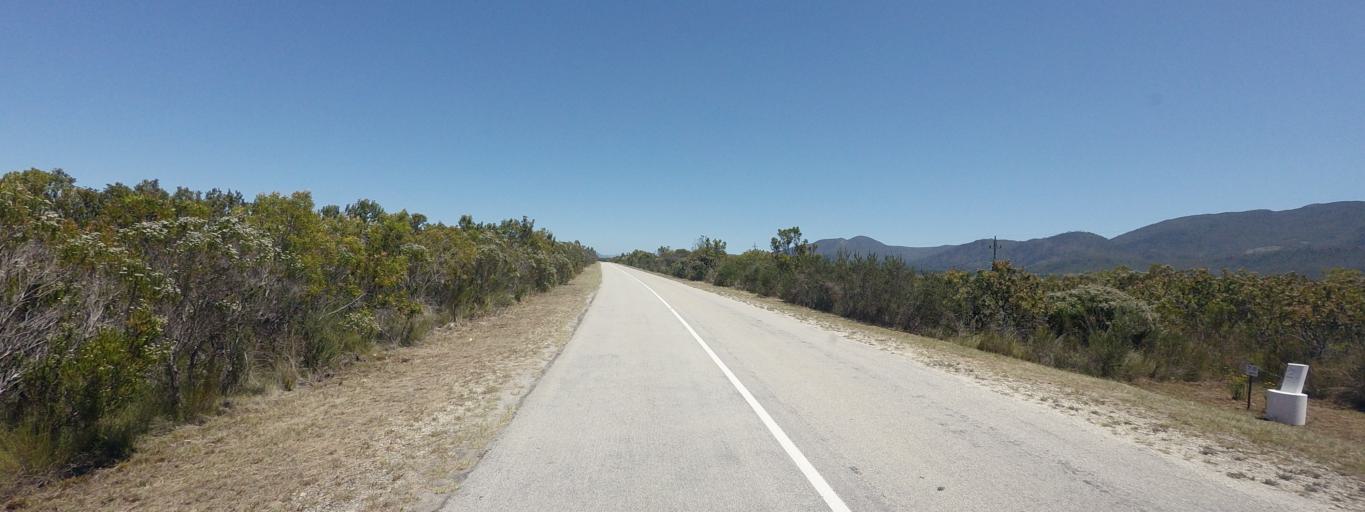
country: ZA
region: Western Cape
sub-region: Eden District Municipality
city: Plettenberg Bay
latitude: -33.9612
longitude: 23.5436
